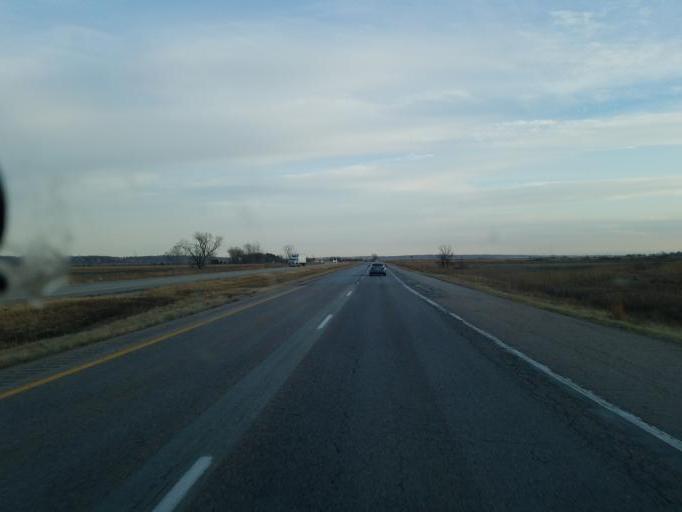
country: US
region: Iowa
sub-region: Harrison County
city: Missouri Valley
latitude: 41.5888
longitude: -95.9494
